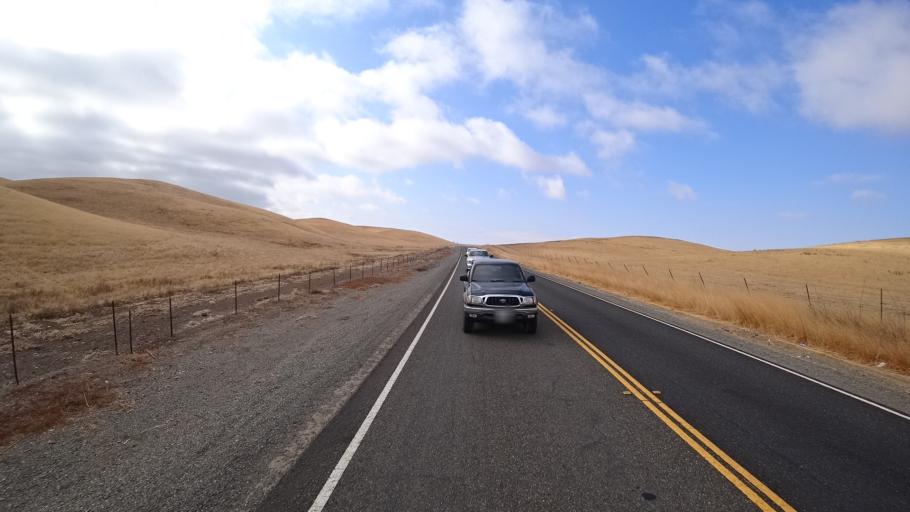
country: US
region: California
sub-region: Yolo County
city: Dunnigan
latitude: 38.7816
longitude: -121.9343
